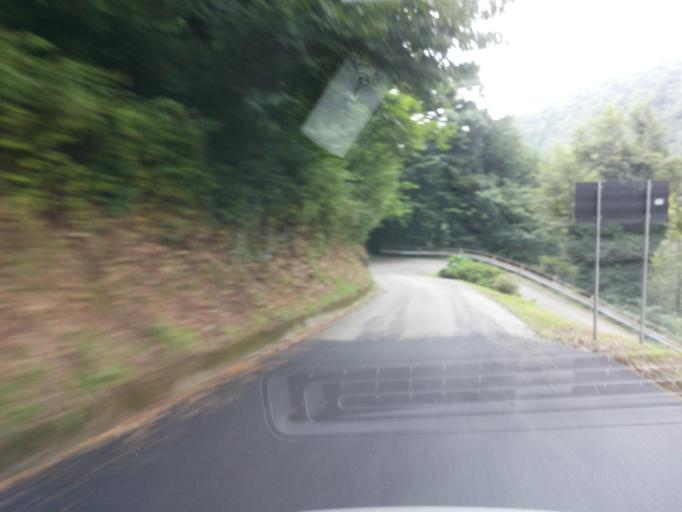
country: IT
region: Piedmont
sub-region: Provincia di Biella
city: San Paolo Cervo
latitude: 45.6458
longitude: 8.0243
